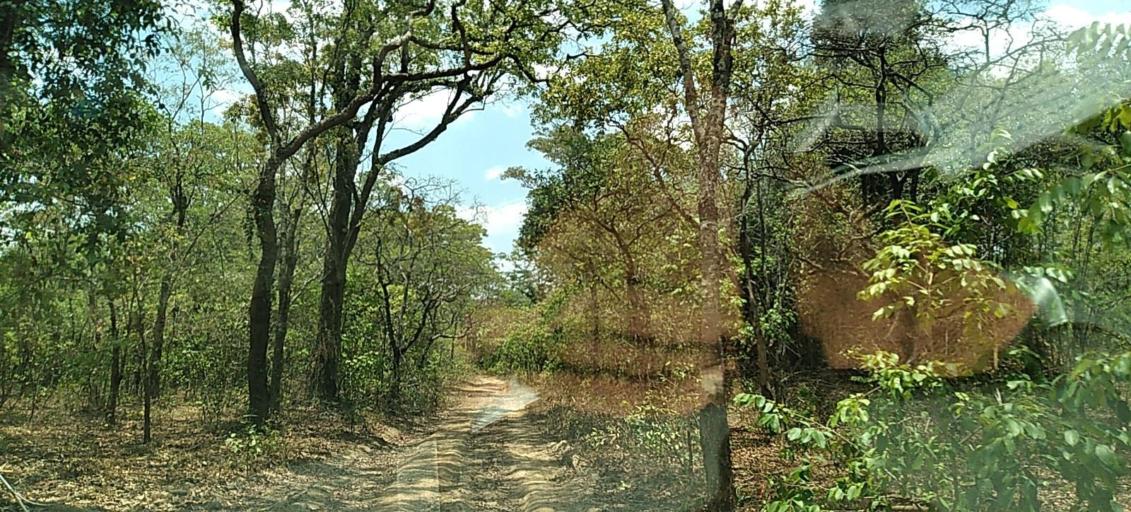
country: ZM
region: Copperbelt
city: Chililabombwe
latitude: -12.4682
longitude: 27.6998
